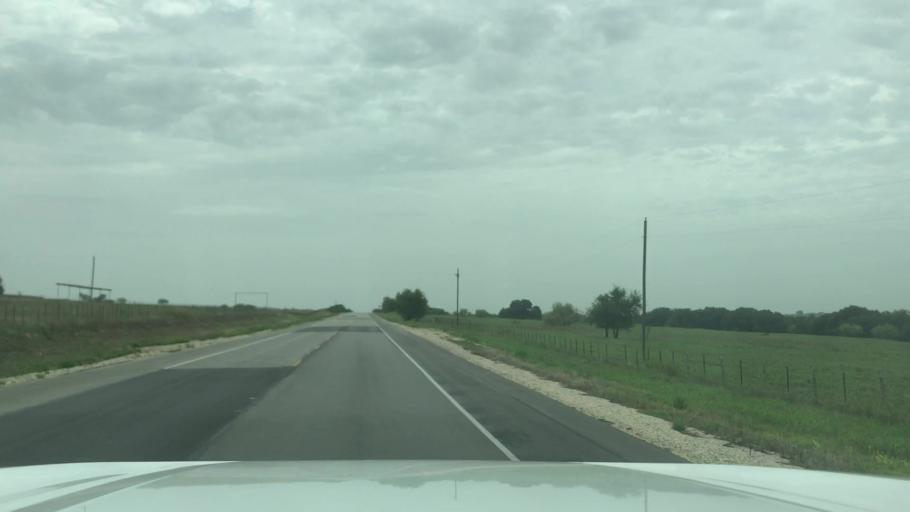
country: US
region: Texas
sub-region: Erath County
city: Dublin
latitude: 32.0673
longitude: -98.2179
